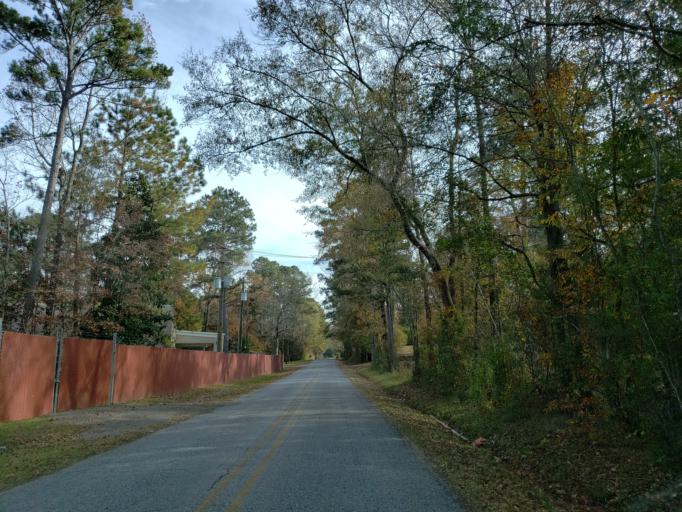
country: US
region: Mississippi
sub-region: Forrest County
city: Rawls Springs
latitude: 31.3756
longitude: -89.3665
